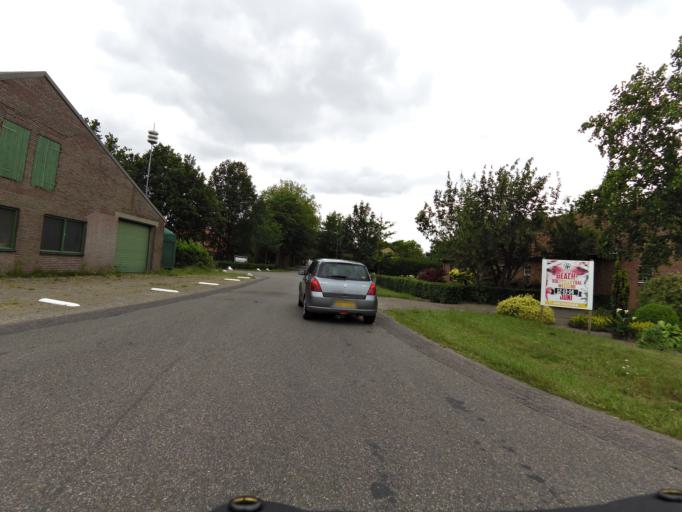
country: NL
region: North Brabant
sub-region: Gemeente Baarle-Nassau
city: Baarle-Nassau
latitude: 51.4446
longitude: 4.9143
